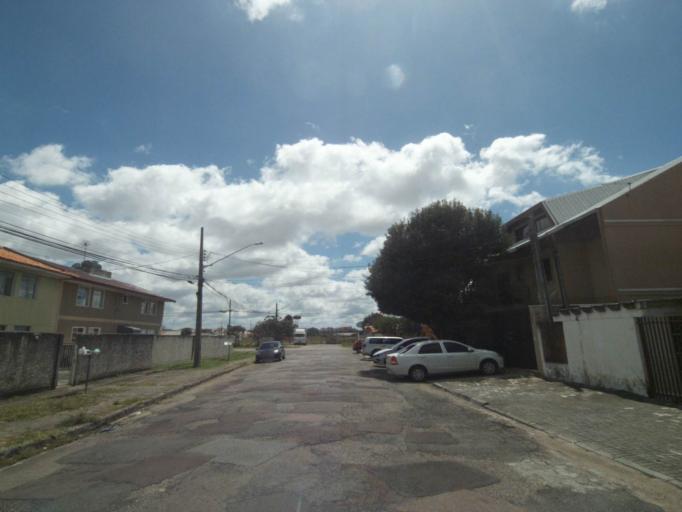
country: BR
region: Parana
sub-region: Pinhais
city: Pinhais
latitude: -25.4406
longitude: -49.2049
